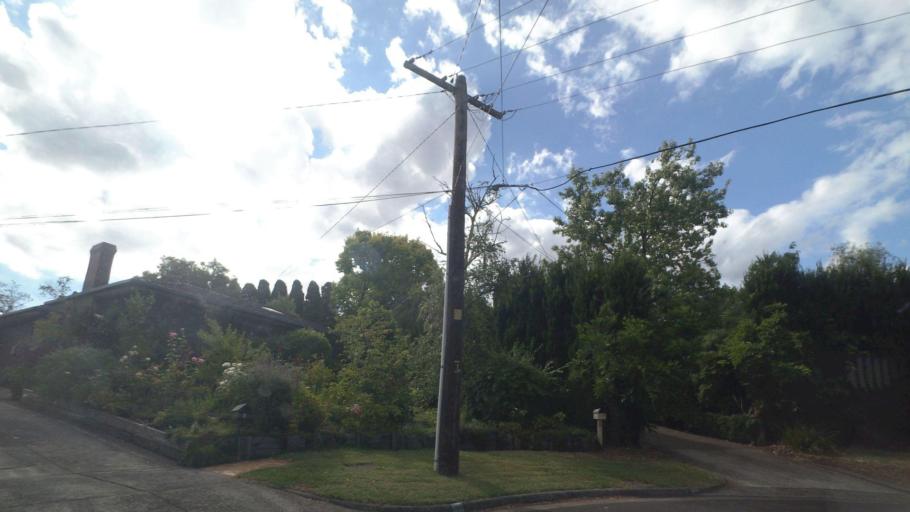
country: AU
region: Victoria
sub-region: Maroondah
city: Warranwood
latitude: -37.7929
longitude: 145.2451
